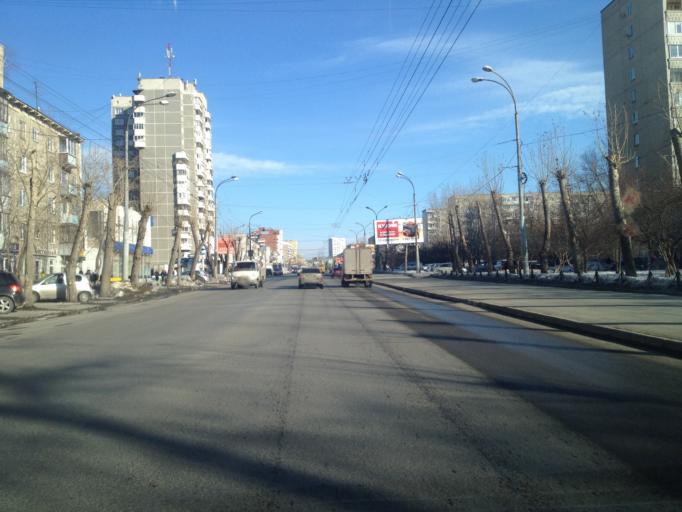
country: RU
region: Sverdlovsk
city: Shirokaya Rechka
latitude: 56.8314
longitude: 60.5412
